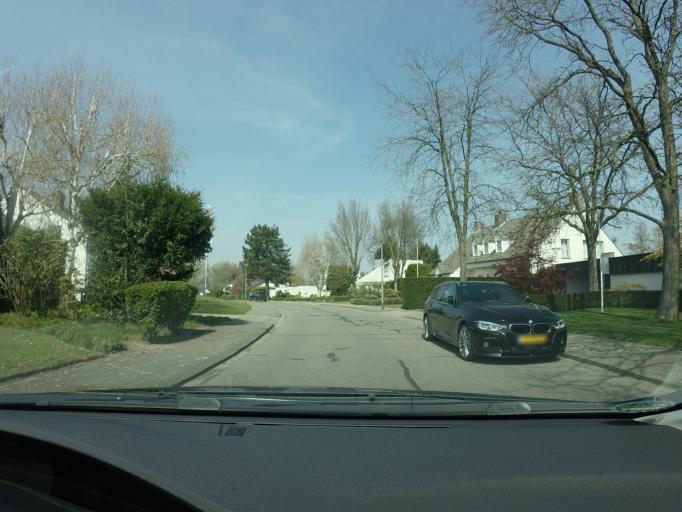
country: NL
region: Limburg
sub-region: Valkenburg aan de Geul
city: Berg
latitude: 50.8327
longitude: 5.7646
